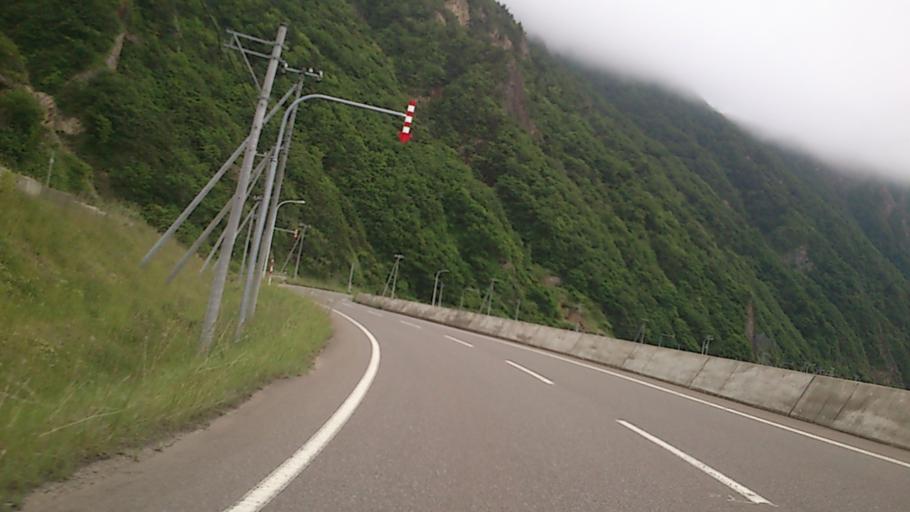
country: JP
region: Hokkaido
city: Kamiiso
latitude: 42.2763
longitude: 139.7849
